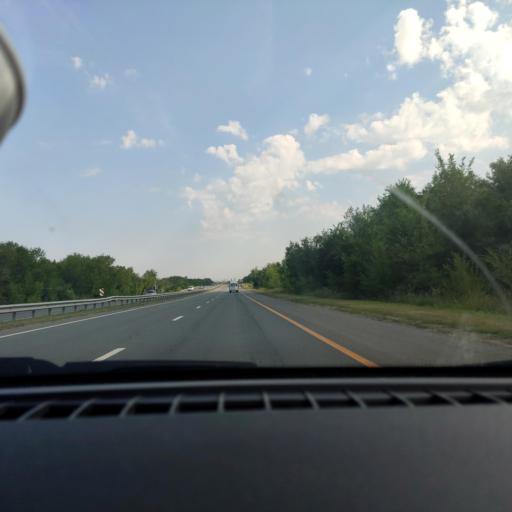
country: RU
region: Samara
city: Novokuybyshevsk
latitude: 53.0407
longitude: 50.0030
